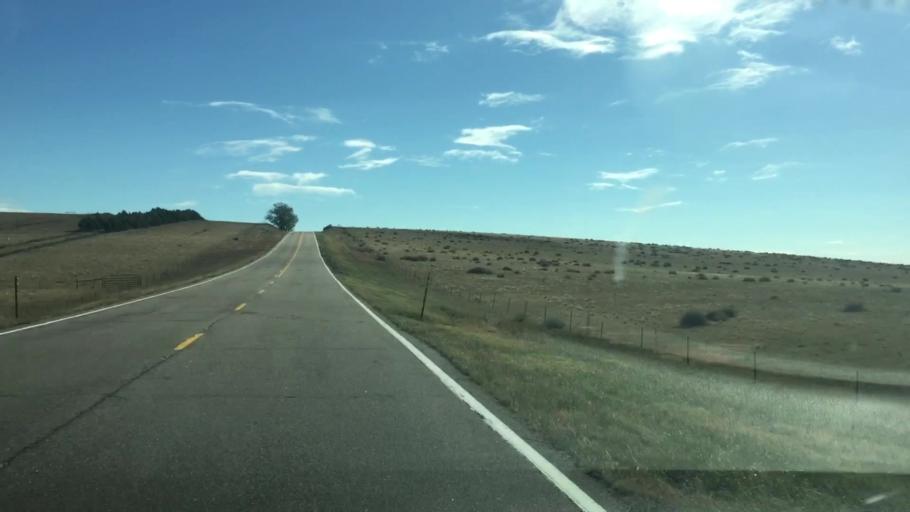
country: US
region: Colorado
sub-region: Elbert County
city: Kiowa
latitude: 39.2736
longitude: -104.2146
